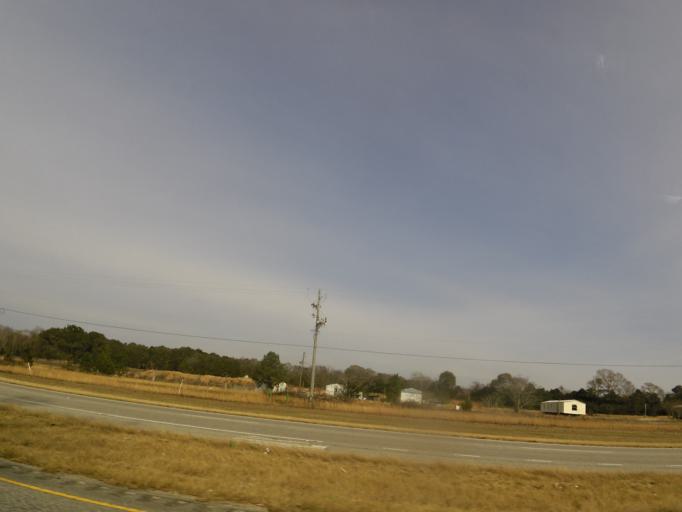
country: US
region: Alabama
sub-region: Dale County
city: Midland City
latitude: 31.3201
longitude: -85.5167
